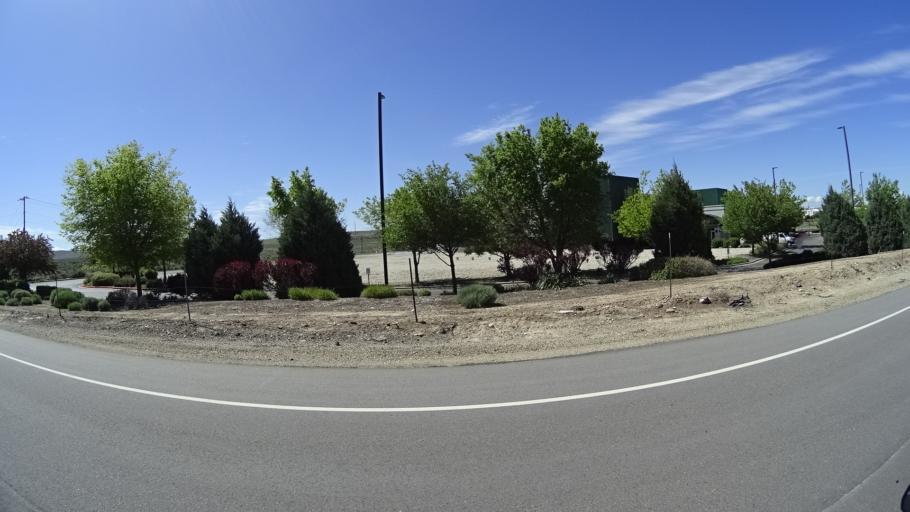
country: US
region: Idaho
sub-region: Ada County
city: Boise
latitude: 43.5311
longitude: -116.1349
